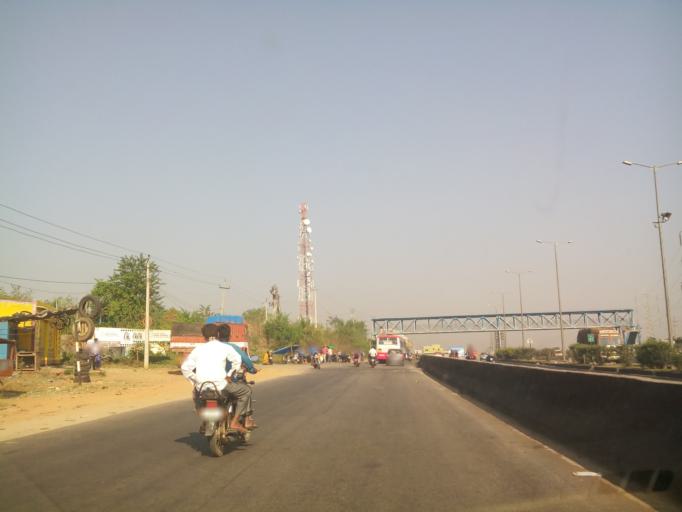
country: IN
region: Karnataka
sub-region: Bangalore Rural
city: Nelamangala
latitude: 13.0944
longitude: 77.3898
